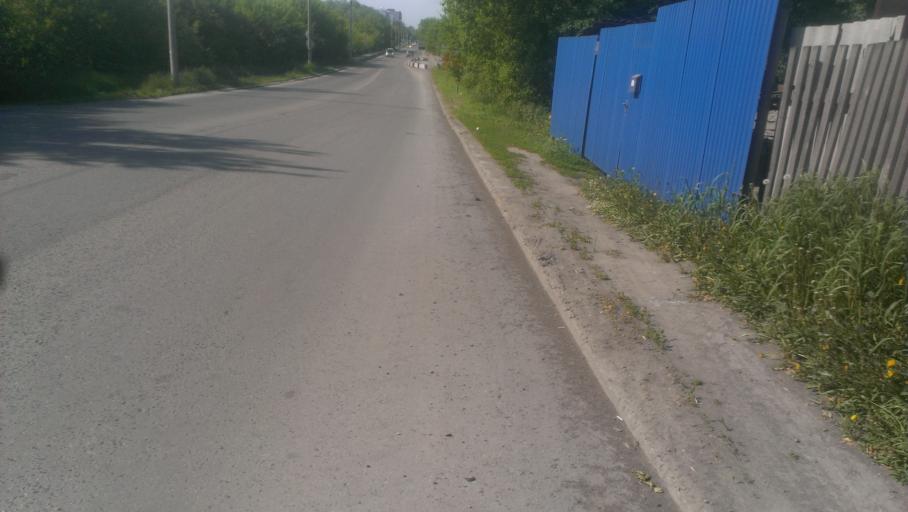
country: RU
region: Altai Krai
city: Novoaltaysk
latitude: 53.4031
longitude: 83.9459
